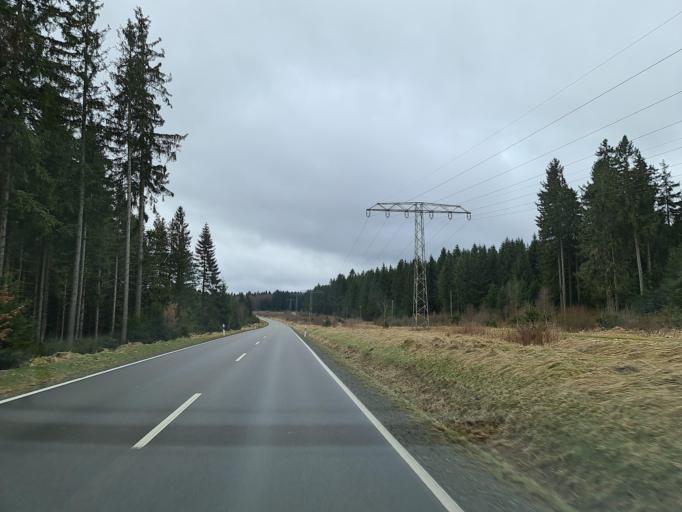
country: DE
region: Saxony
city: Grunbach
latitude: 50.4339
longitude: 12.3677
